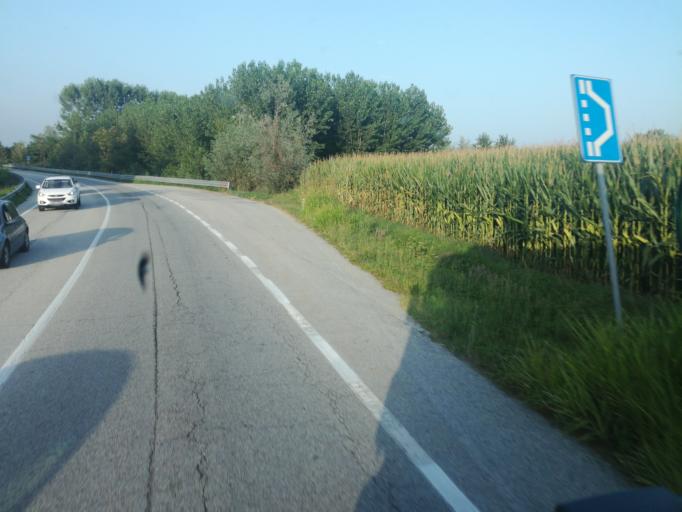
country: IT
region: Piedmont
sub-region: Provincia di Torino
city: Osasco
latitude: 44.8376
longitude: 7.3300
